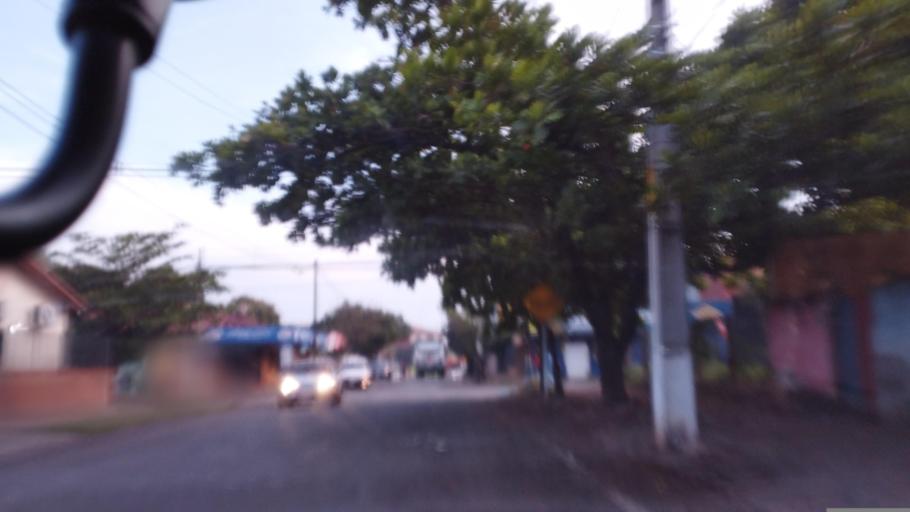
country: PY
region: Central
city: Fernando de la Mora
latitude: -25.3022
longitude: -57.5303
